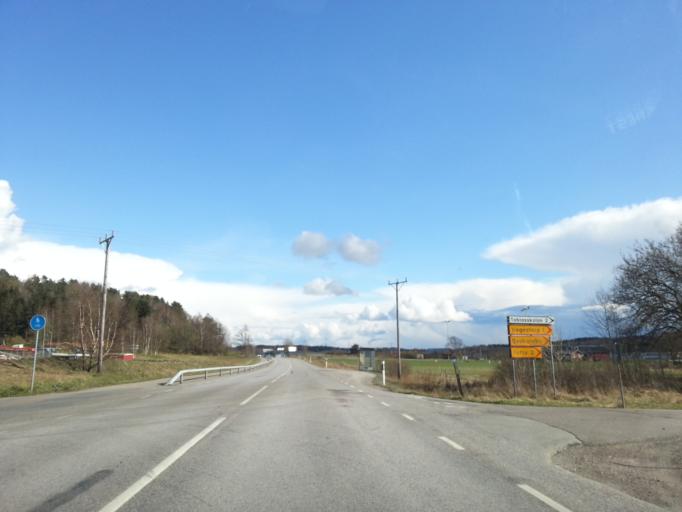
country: SE
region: Vaestra Goetaland
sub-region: Kungalvs Kommun
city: Kungalv
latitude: 57.9019
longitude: 11.9281
